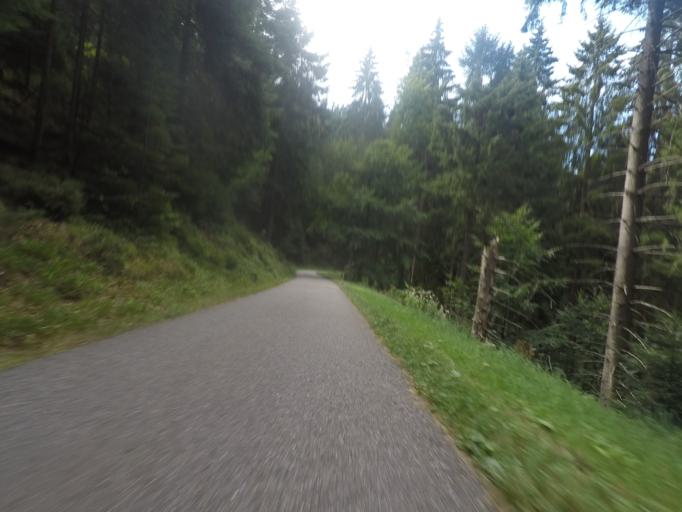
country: DE
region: Baden-Wuerttemberg
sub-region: Karlsruhe Region
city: Bad Herrenalb
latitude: 48.7670
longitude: 8.4618
